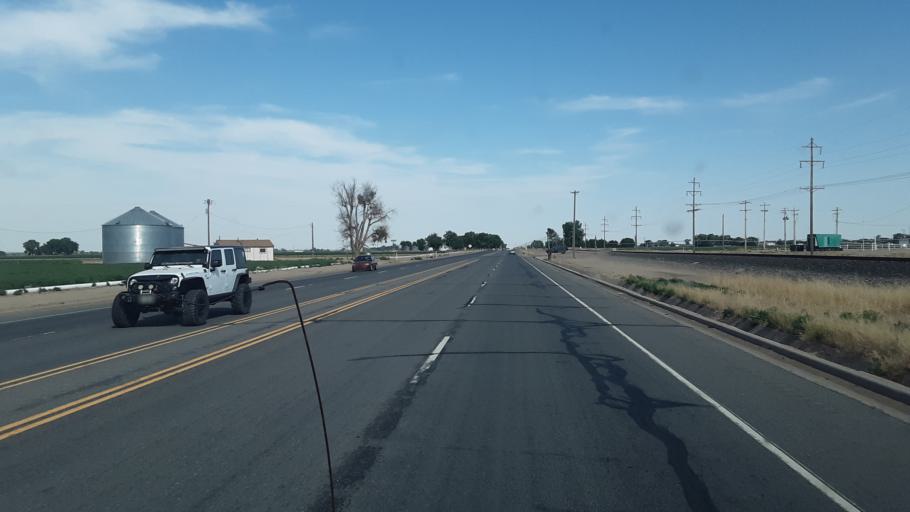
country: US
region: Colorado
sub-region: Otero County
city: Rocky Ford
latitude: 38.0796
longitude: -103.7859
